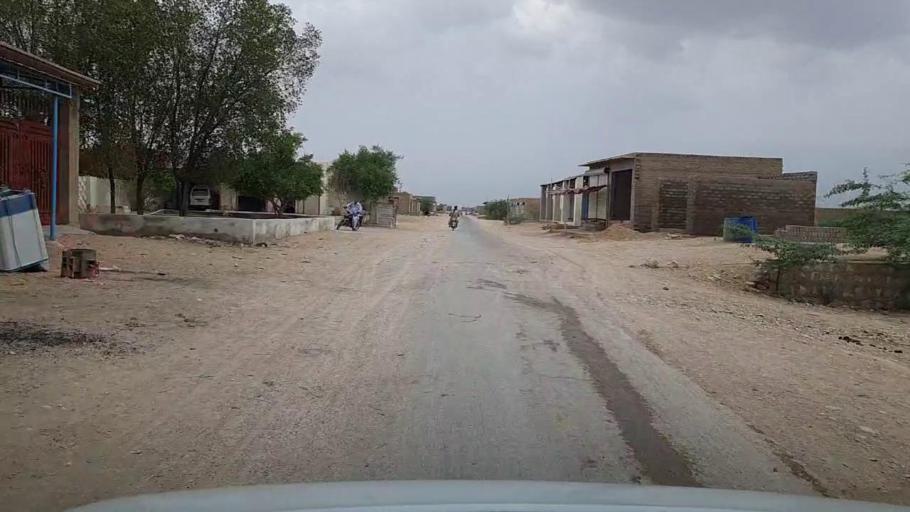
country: PK
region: Sindh
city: Sehwan
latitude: 26.3375
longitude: 67.7230
